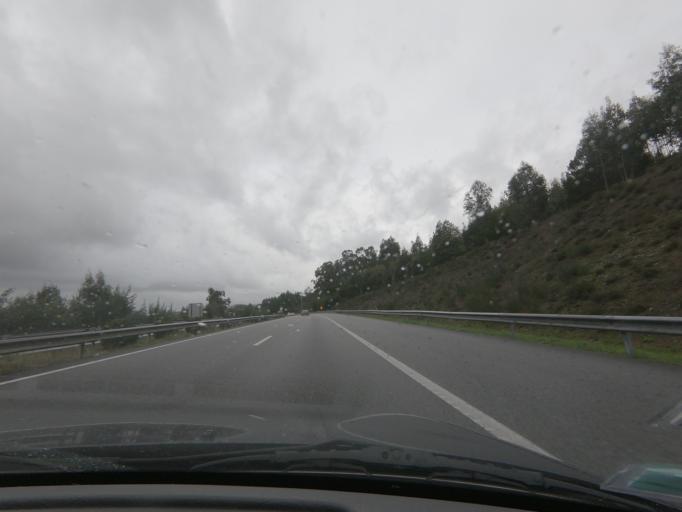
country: PT
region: Porto
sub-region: Valongo
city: Campo
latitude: 41.1941
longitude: -8.4841
